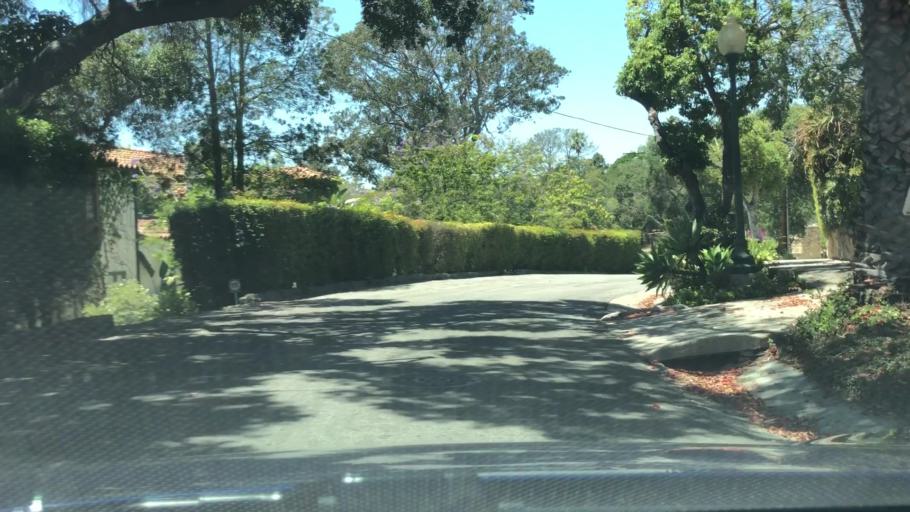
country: US
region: California
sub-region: Santa Barbara County
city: Mission Canyon
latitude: 34.4389
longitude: -119.7006
